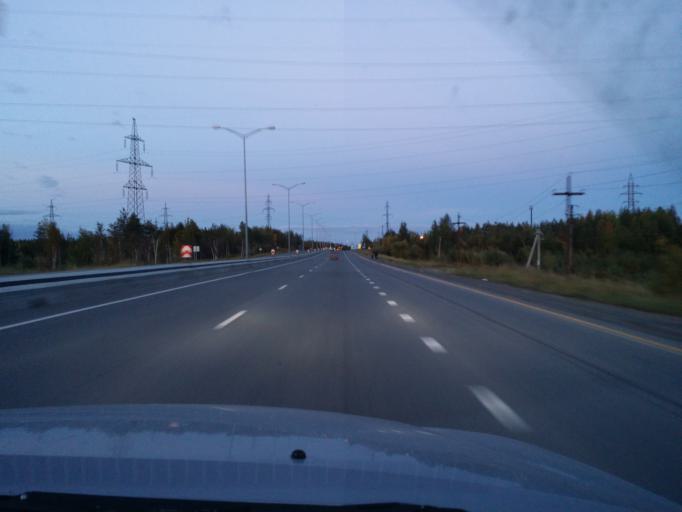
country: RU
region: Khanty-Mansiyskiy Avtonomnyy Okrug
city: Nizhnevartovsk
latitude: 60.9875
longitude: 76.4509
